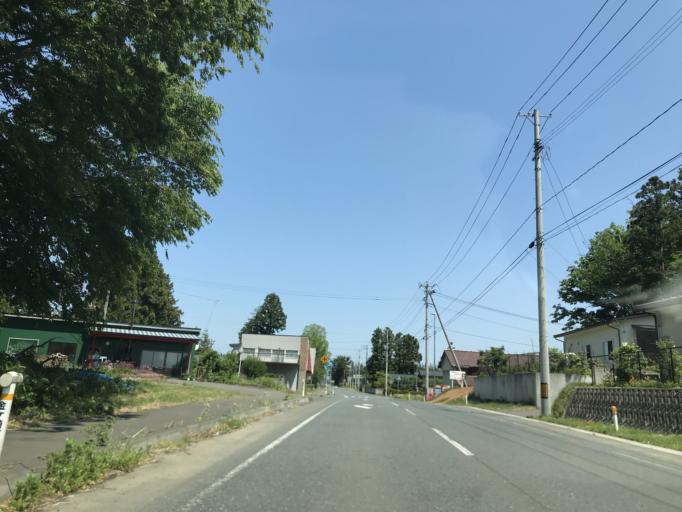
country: JP
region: Iwate
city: Kitakami
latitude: 39.2406
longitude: 141.0667
